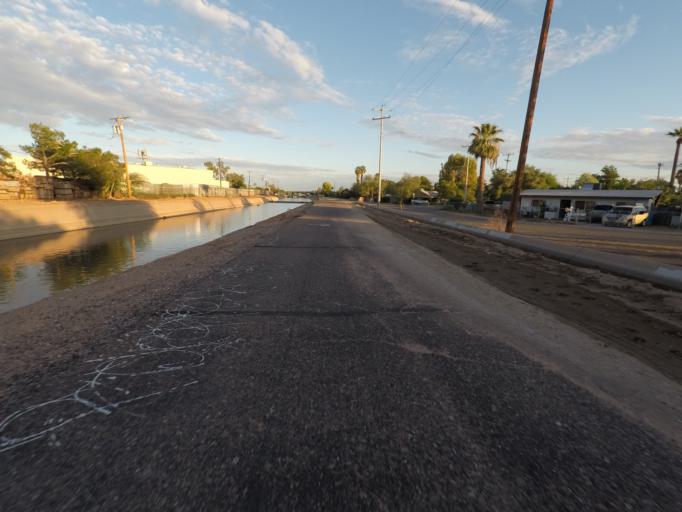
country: US
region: Arizona
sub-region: Maricopa County
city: Phoenix
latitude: 33.4651
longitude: -112.0155
